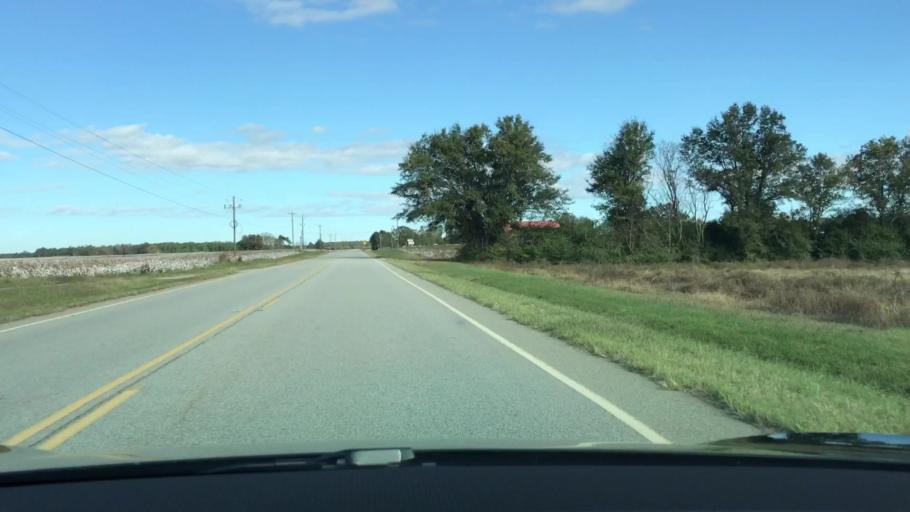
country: US
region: Georgia
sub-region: Jefferson County
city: Wrens
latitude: 33.1449
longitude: -82.4569
